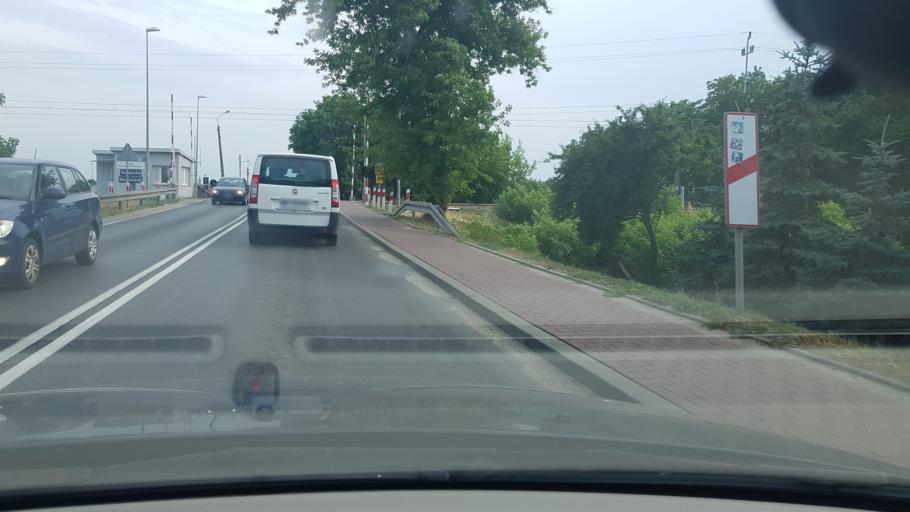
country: PL
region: Lodz Voivodeship
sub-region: Powiat tomaszowski
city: Tomaszow Mazowiecki
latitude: 51.5551
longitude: 20.0182
